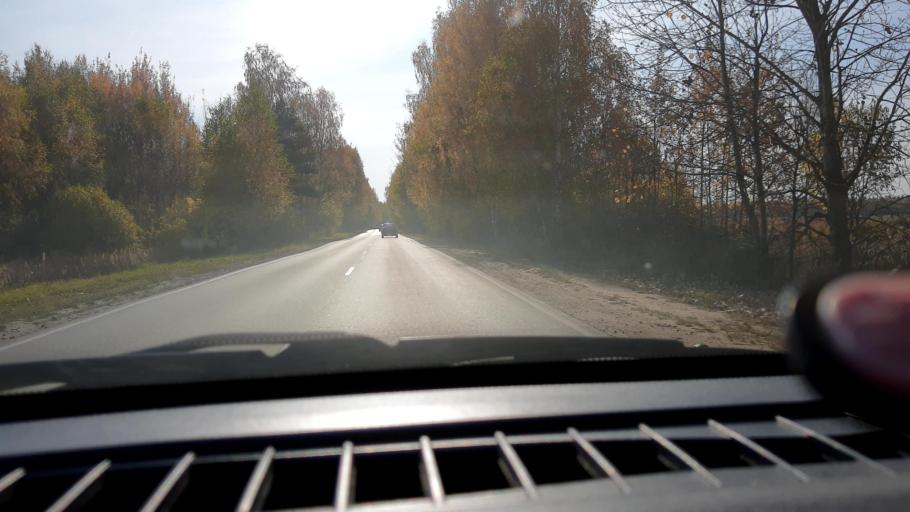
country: RU
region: Nizjnij Novgorod
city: Neklyudovo
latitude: 56.5255
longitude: 43.8333
